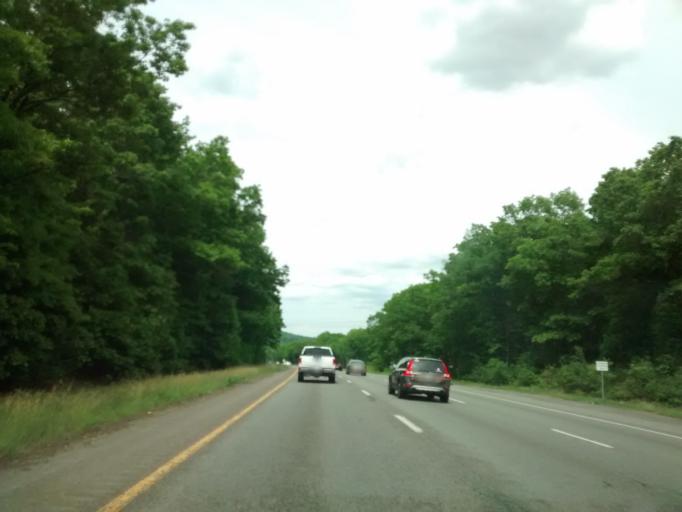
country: US
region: Massachusetts
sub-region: Worcester County
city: Shrewsbury
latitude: 42.2978
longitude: -71.7431
